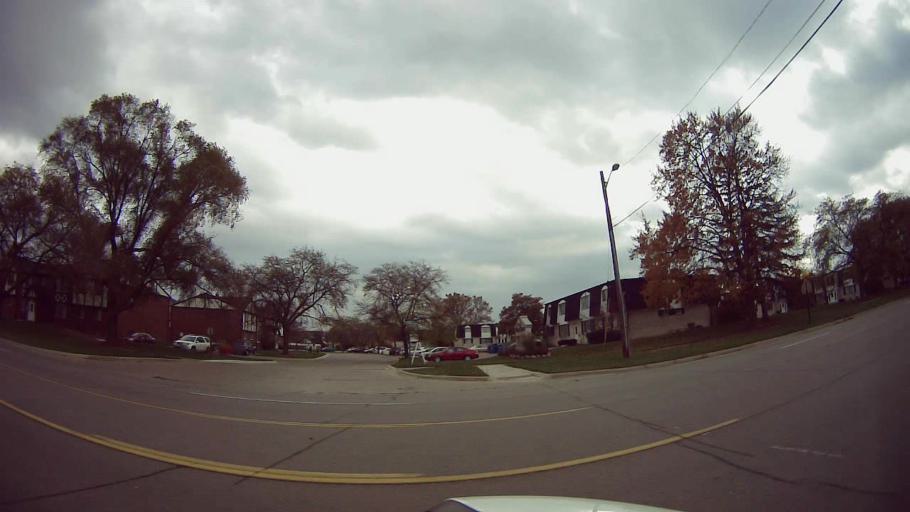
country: US
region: Michigan
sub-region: Macomb County
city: Sterling Heights
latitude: 42.5513
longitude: -83.0229
